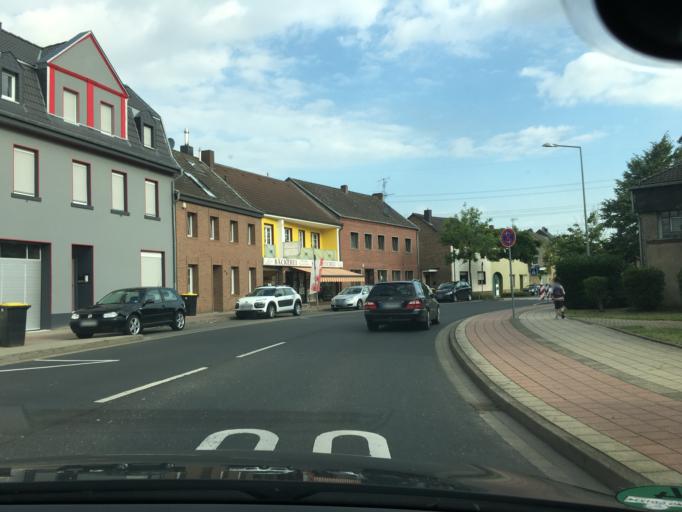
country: DE
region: North Rhine-Westphalia
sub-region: Regierungsbezirk Koln
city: Niederzier
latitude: 50.8315
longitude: 6.4416
